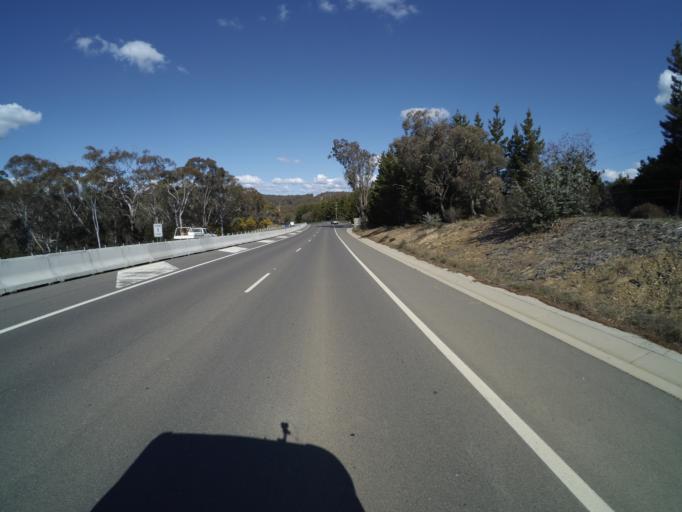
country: AU
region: New South Wales
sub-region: Queanbeyan
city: Queanbeyan
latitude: -35.3435
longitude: 149.2648
